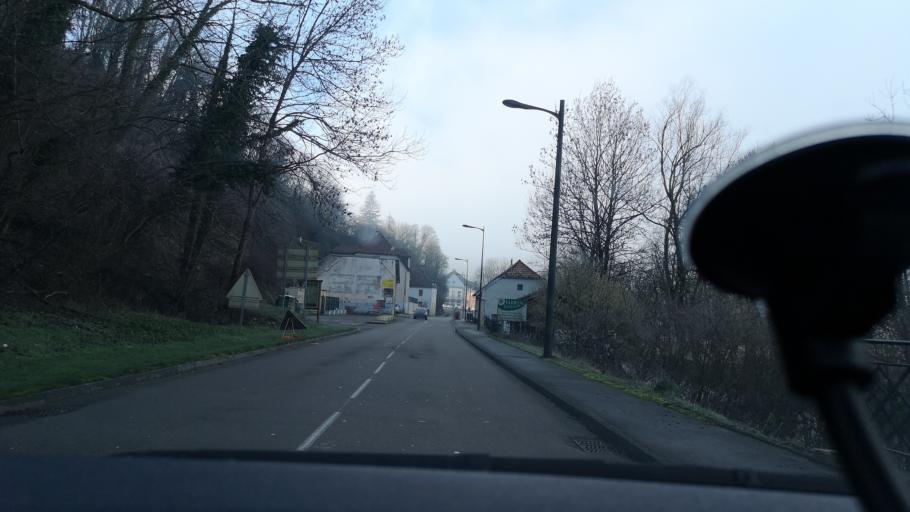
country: FR
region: Franche-Comte
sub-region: Departement du Doubs
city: Clerval
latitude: 47.3950
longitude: 6.5009
